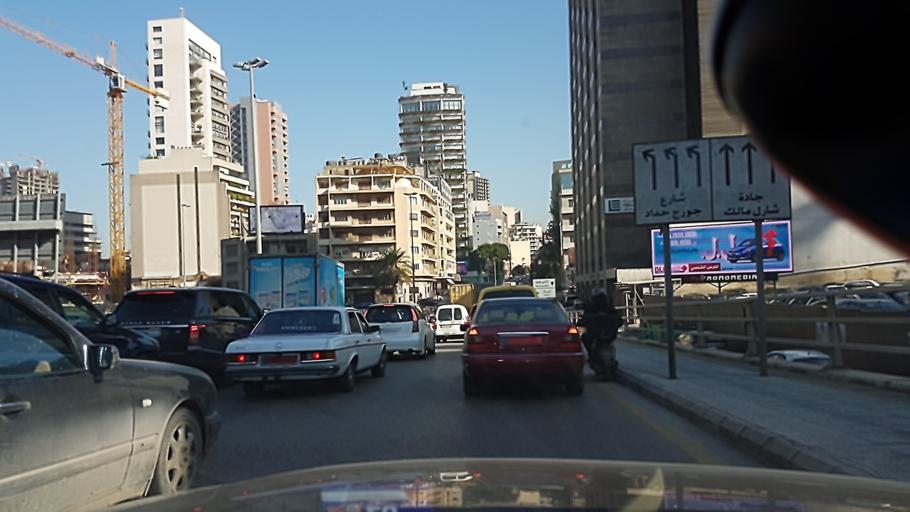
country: LB
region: Beyrouth
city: Beirut
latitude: 33.8923
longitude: 35.5084
